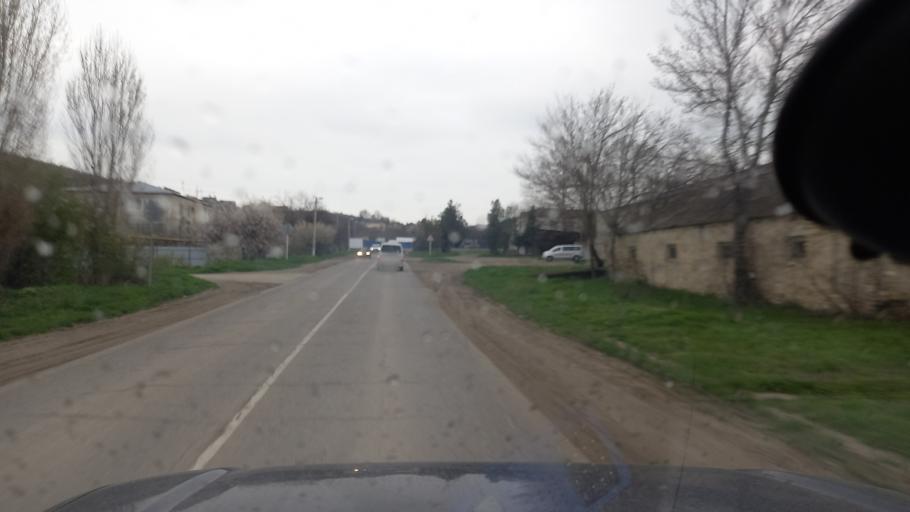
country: RU
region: Krasnodarskiy
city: Anapskaya
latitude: 44.8617
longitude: 37.4400
